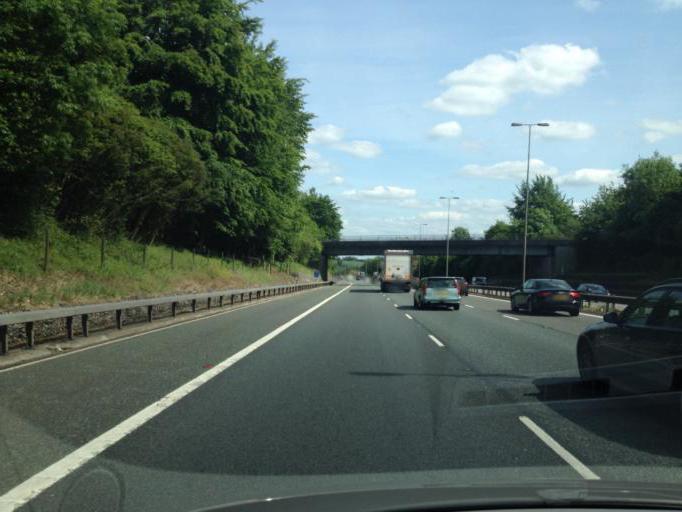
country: GB
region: England
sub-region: Buckinghamshire
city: Marlow
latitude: 51.6129
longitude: -0.7977
